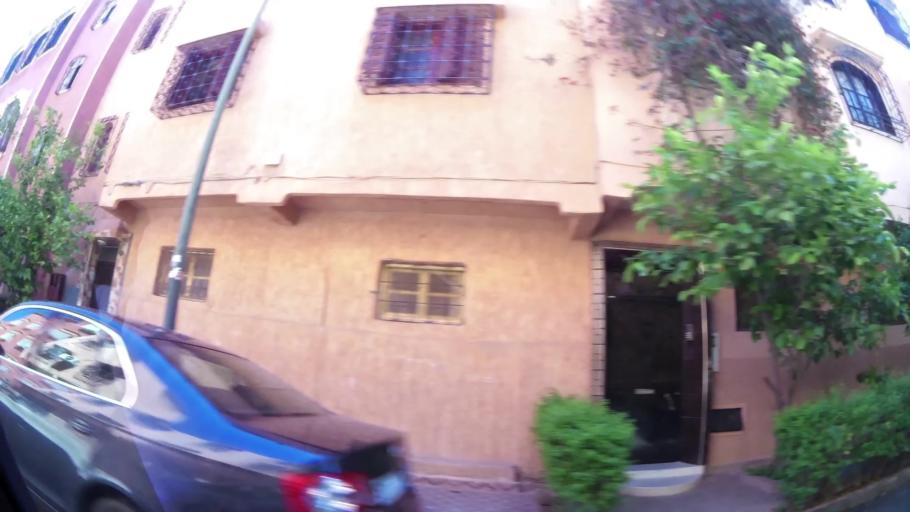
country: MA
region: Marrakech-Tensift-Al Haouz
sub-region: Marrakech
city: Marrakesh
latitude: 31.6551
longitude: -7.9861
